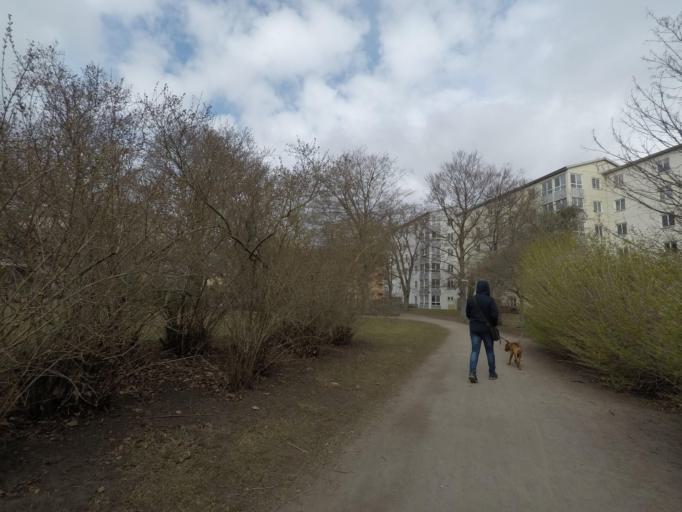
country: SE
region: Skane
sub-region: Malmo
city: Malmoe
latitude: 55.6040
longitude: 13.0344
